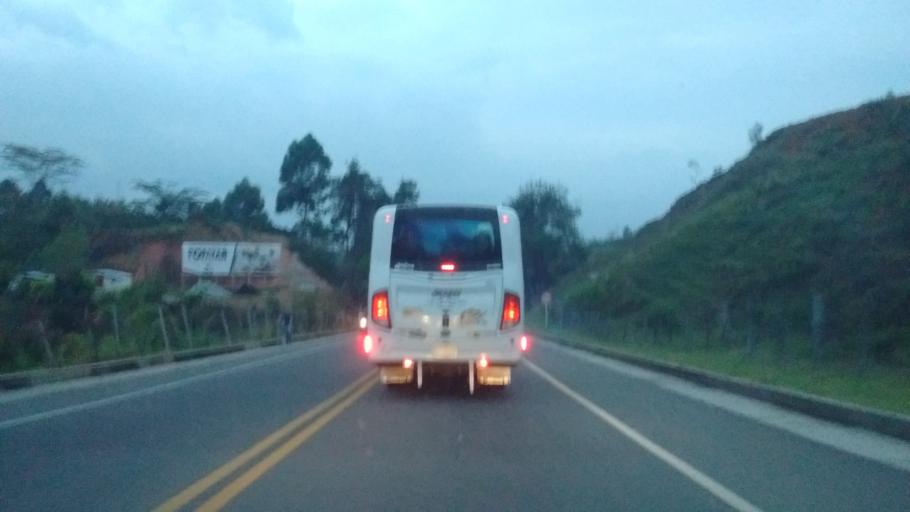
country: CO
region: Cauca
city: Popayan
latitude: 2.4214
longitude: -76.6320
